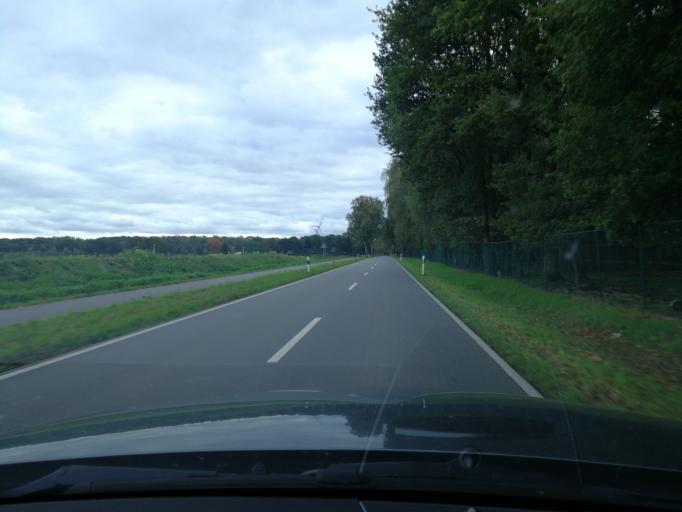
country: NL
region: Limburg
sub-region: Gemeente Venlo
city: Arcen
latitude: 51.4835
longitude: 6.2197
